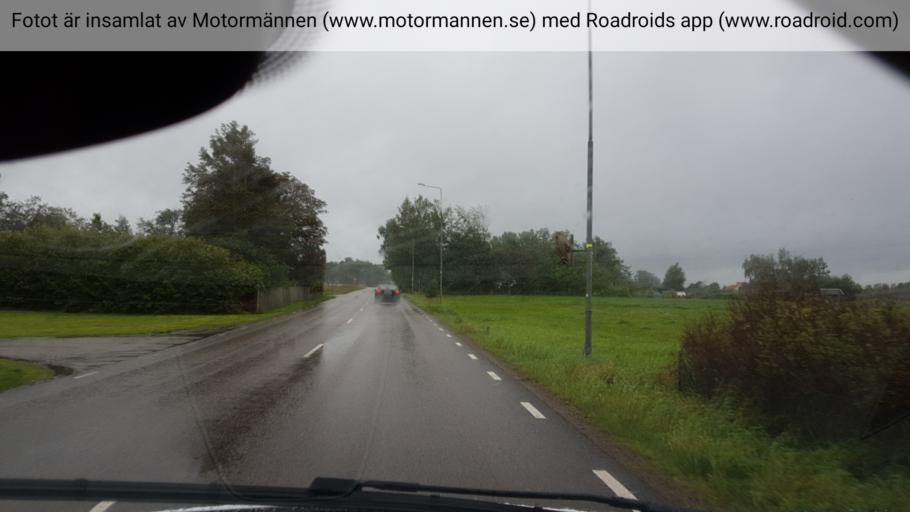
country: SE
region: Halland
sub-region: Laholms Kommun
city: Laholm
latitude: 56.4935
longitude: 13.0359
